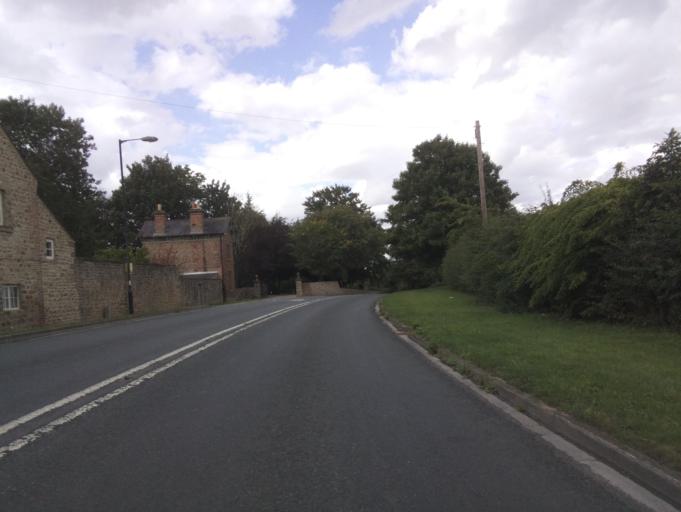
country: GB
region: England
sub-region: North Yorkshire
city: Ripon
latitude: 54.1825
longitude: -1.5610
